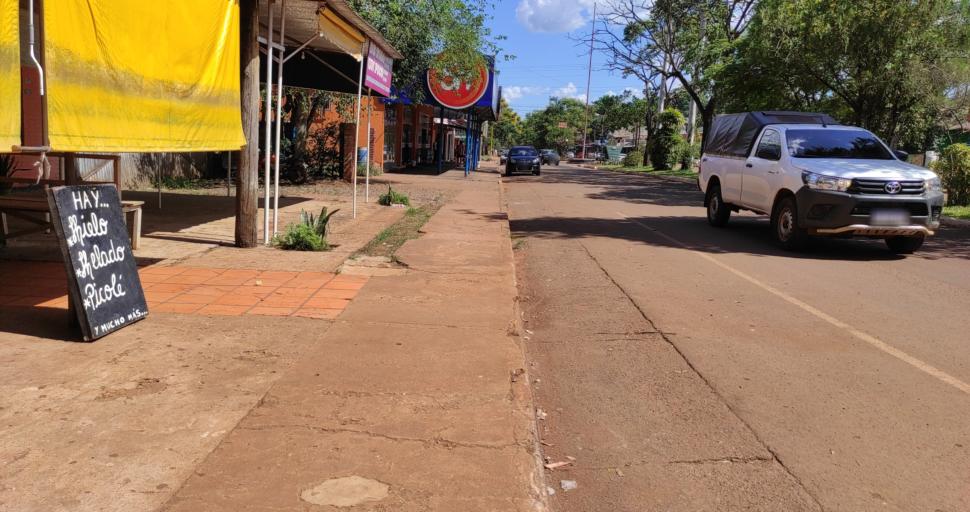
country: AR
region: Misiones
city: El Soberbio
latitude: -27.2958
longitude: -54.1980
